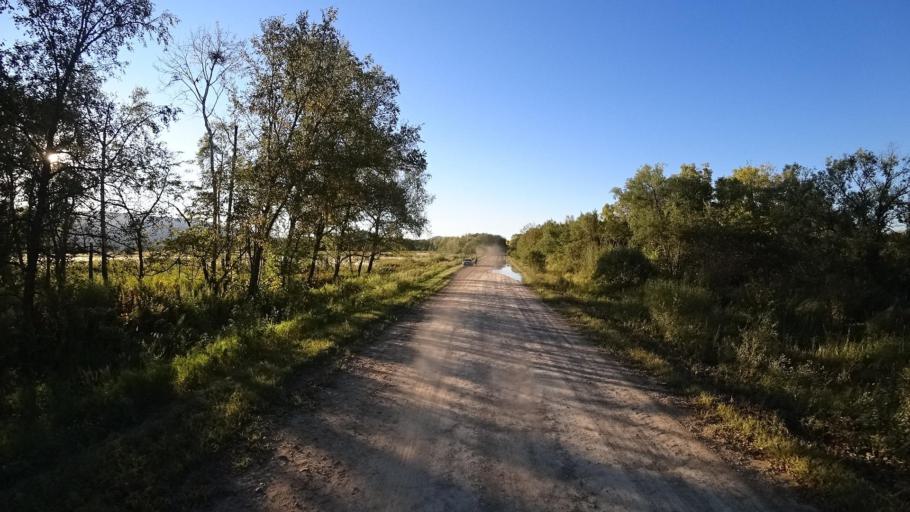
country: RU
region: Primorskiy
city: Kirovskiy
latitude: 44.8158
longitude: 133.6114
